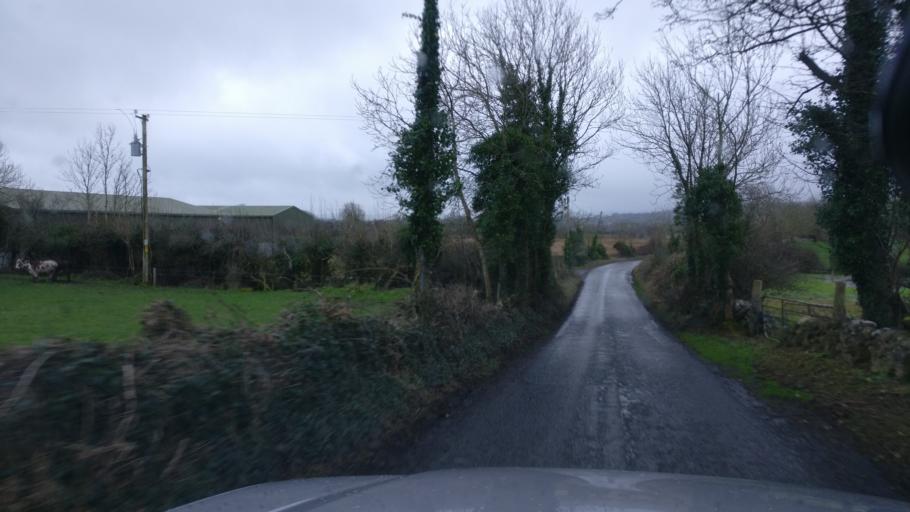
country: IE
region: Connaught
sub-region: County Galway
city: Loughrea
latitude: 53.1982
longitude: -8.6636
